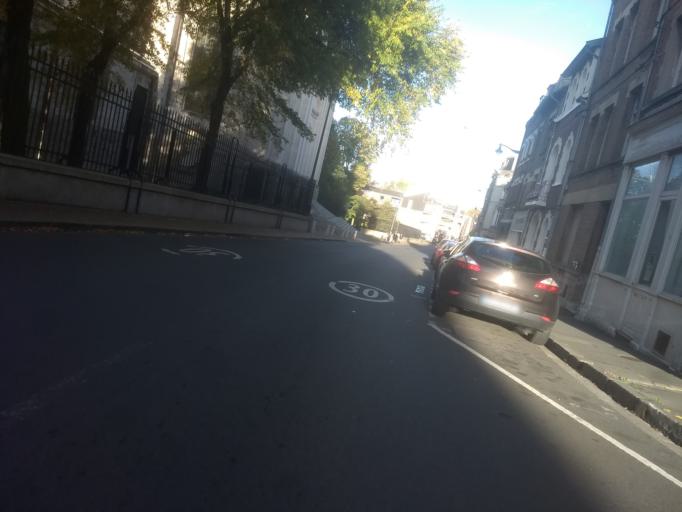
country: FR
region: Nord-Pas-de-Calais
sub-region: Departement du Pas-de-Calais
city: Arras
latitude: 50.2930
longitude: 2.7758
